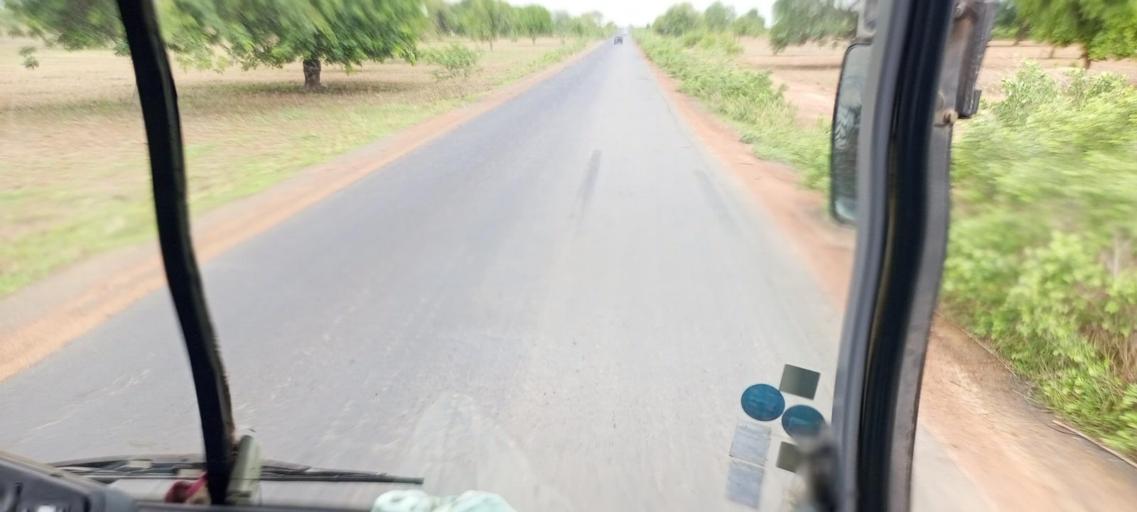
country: ML
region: Segou
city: Bla
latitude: 12.7653
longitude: -5.7403
